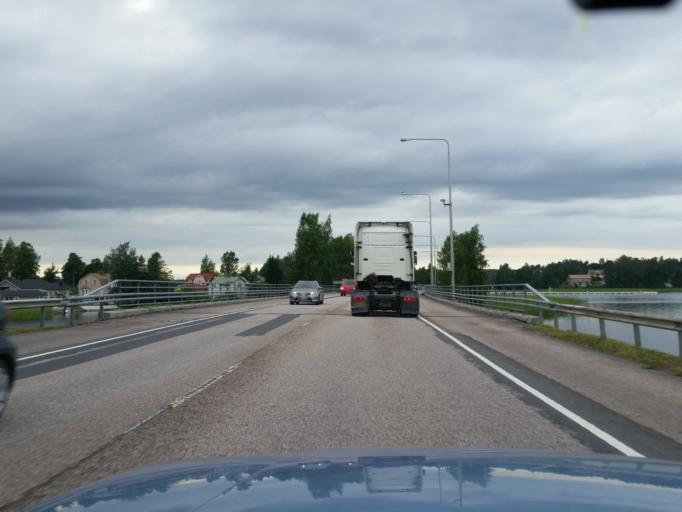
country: FI
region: Uusimaa
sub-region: Raaseporin
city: Ekenaes
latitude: 59.9821
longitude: 23.4363
